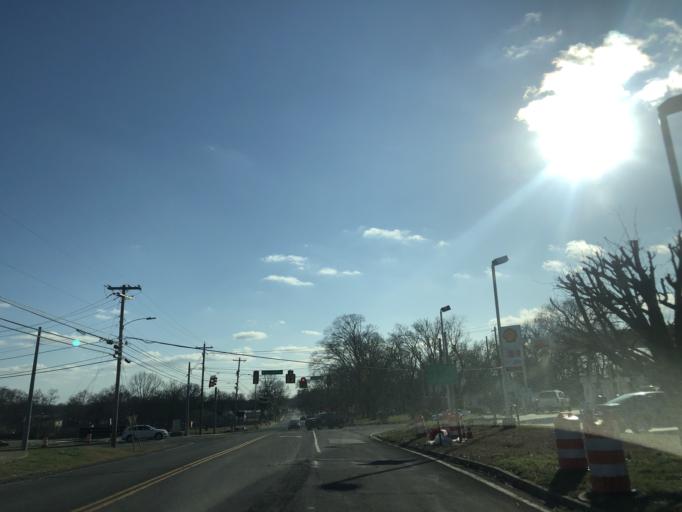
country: US
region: Tennessee
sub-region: Sumner County
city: Gallatin
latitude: 36.4053
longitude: -86.4449
